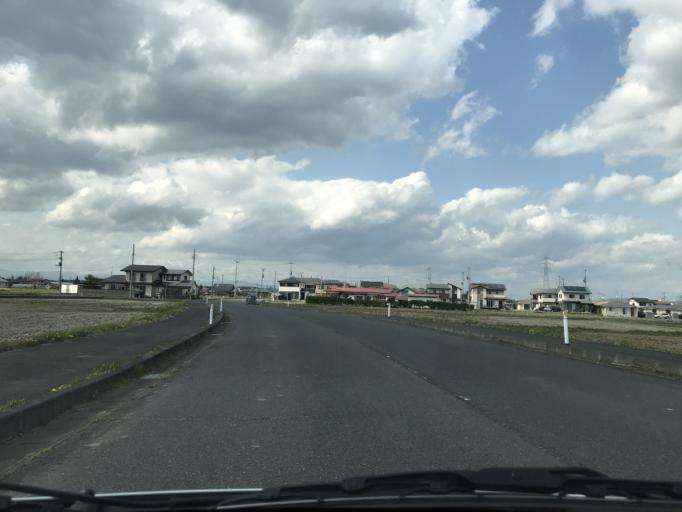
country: JP
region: Iwate
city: Mizusawa
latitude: 39.1587
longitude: 141.1229
